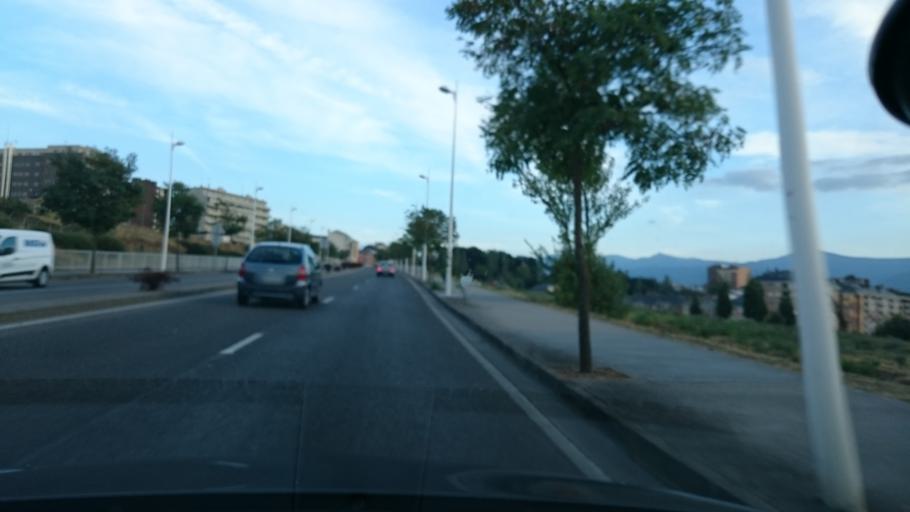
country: ES
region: Castille and Leon
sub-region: Provincia de Leon
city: Ponferrada
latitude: 42.5551
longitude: -6.5870
